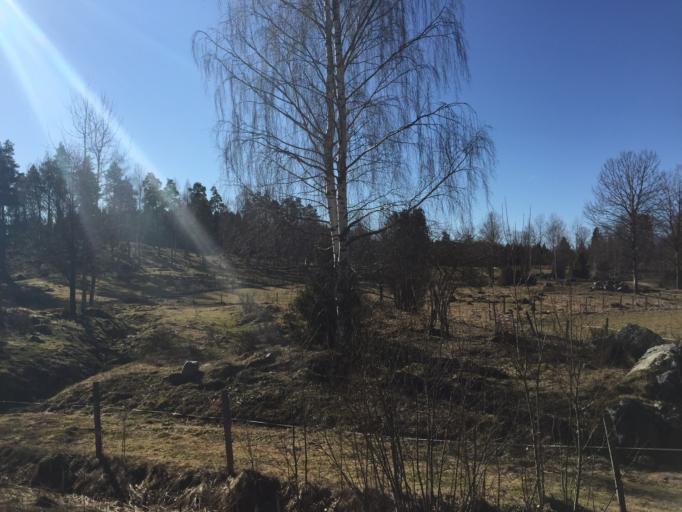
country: SE
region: OEstergoetland
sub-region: Finspangs Kommun
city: Finspang
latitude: 58.7865
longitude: 15.7677
